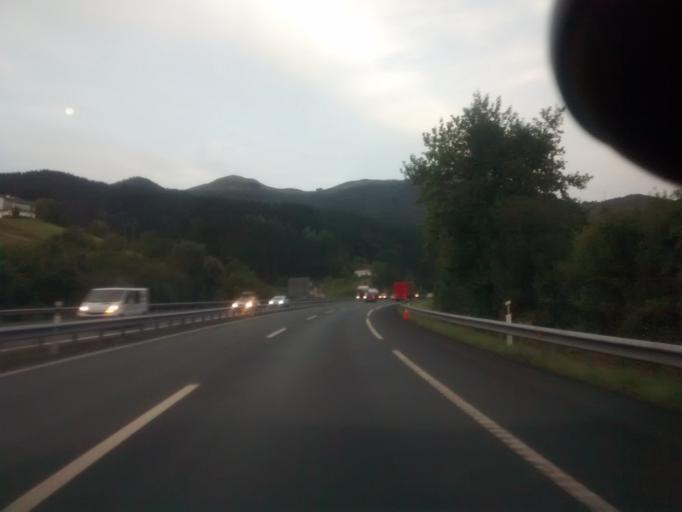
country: ES
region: Basque Country
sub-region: Provincia de Guipuzcoa
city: Cestona
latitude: 43.2594
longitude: -2.2862
